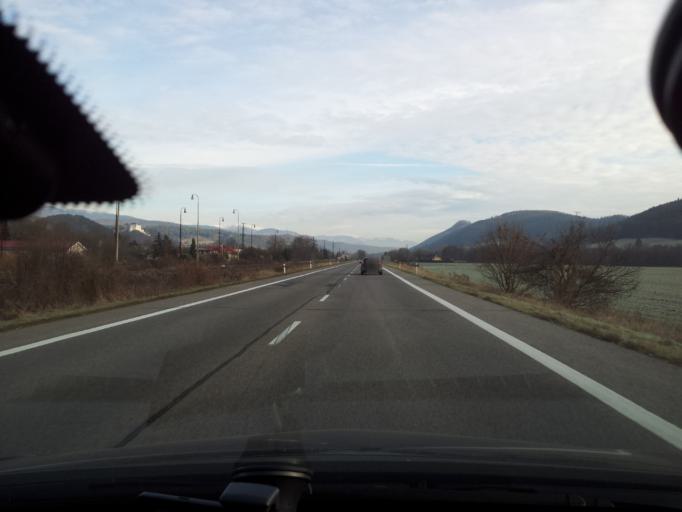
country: SK
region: Banskobystricky
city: Hrochot,Slovakia
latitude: 48.7578
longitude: 19.2653
